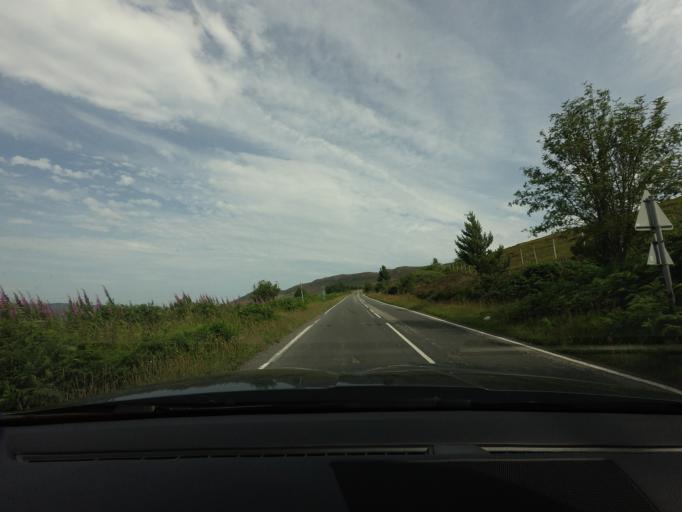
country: GB
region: Scotland
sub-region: Highland
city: Alness
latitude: 57.8433
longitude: -4.2872
